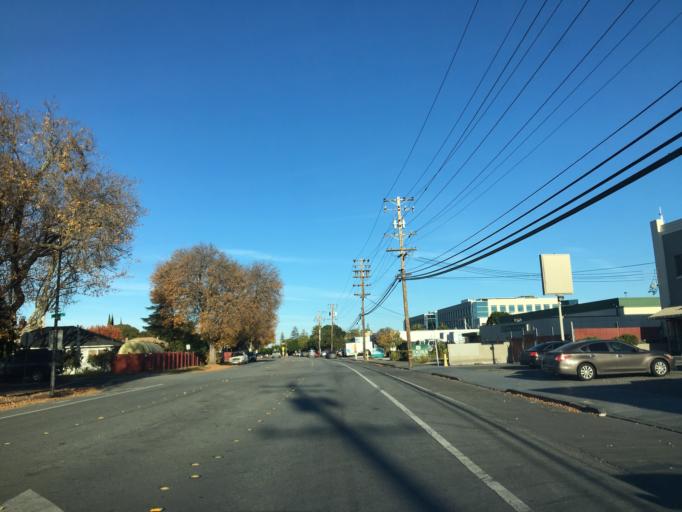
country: US
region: California
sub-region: San Mateo County
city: Redwood City
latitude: 37.4960
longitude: -122.2384
